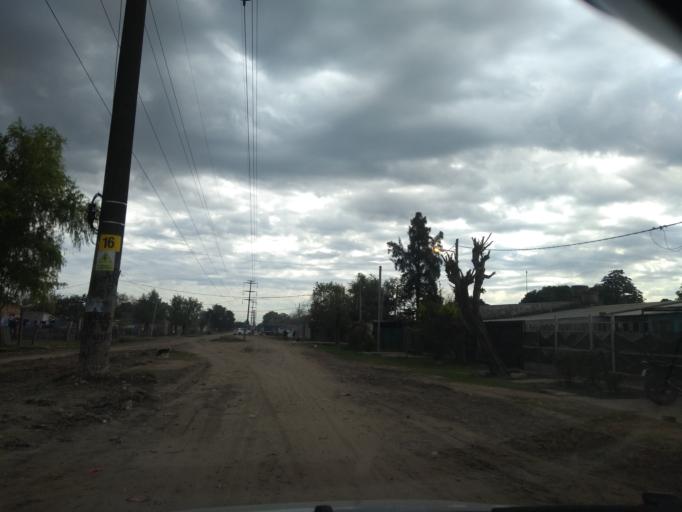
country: AR
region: Chaco
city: Barranqueras
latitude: -27.4751
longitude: -58.9163
